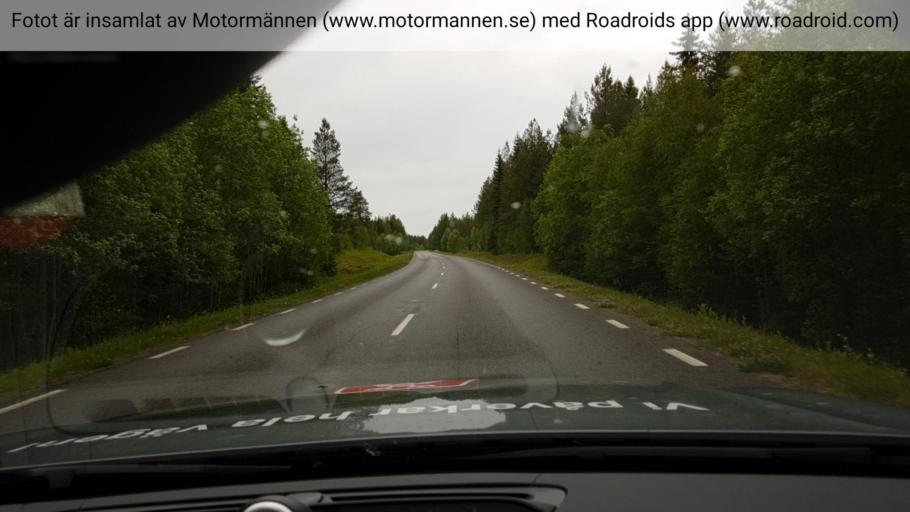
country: SE
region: Jaemtland
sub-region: Stroemsunds Kommun
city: Stroemsund
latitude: 63.6011
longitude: 15.3052
